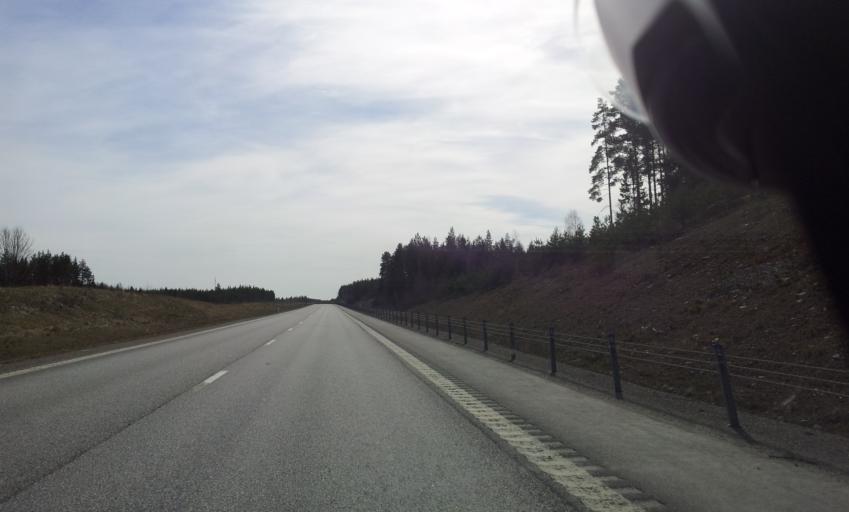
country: SE
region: Uppsala
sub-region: Tierps Kommun
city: Tierp
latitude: 60.2535
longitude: 17.5000
